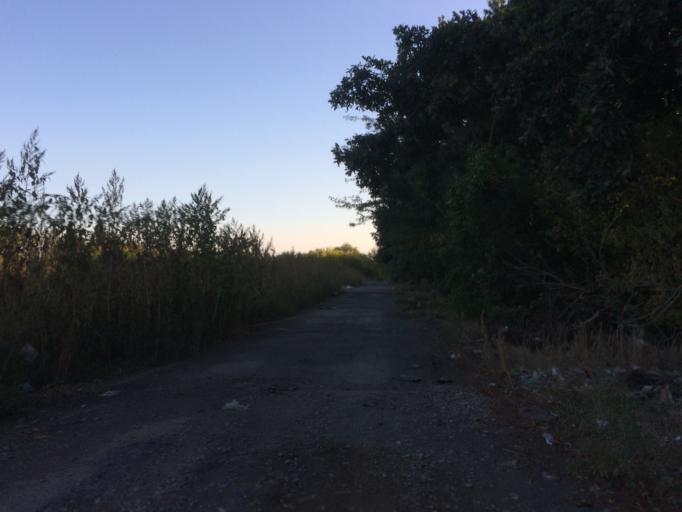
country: RU
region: Rostov
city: Gigant
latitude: 46.5158
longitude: 41.1947
